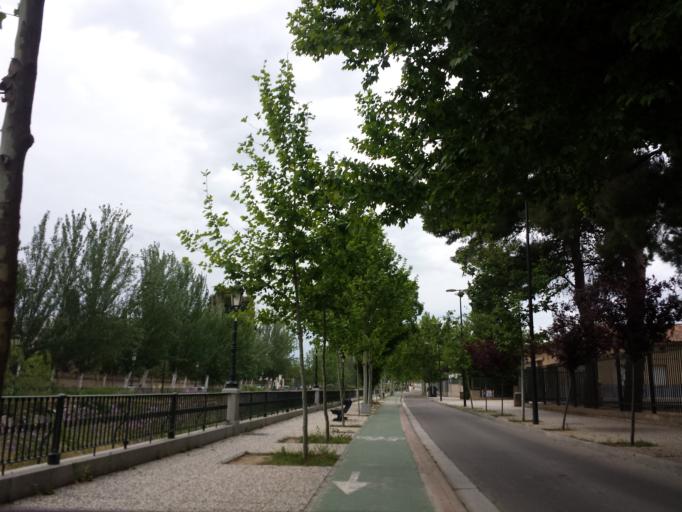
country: ES
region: Aragon
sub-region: Provincia de Zaragoza
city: Delicias
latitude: 41.6254
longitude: -0.9069
